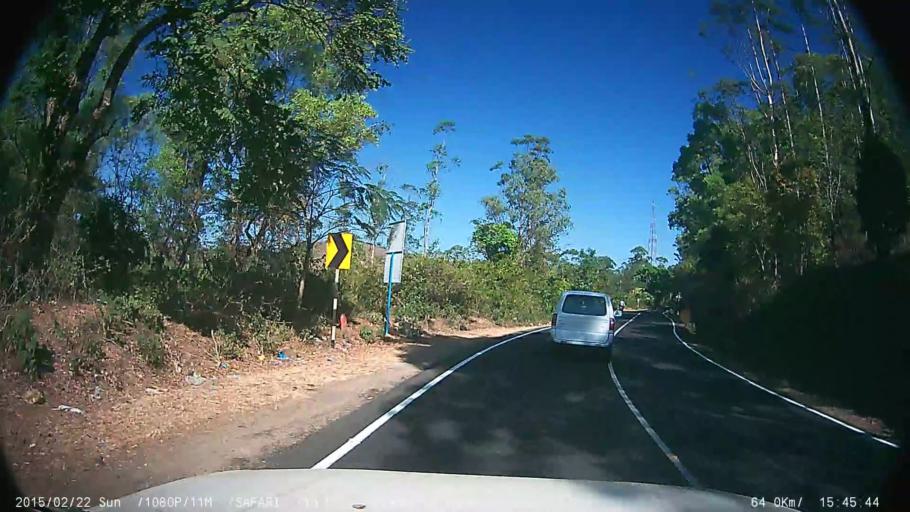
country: IN
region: Kerala
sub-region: Kottayam
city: Erattupetta
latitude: 9.5812
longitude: 76.9796
